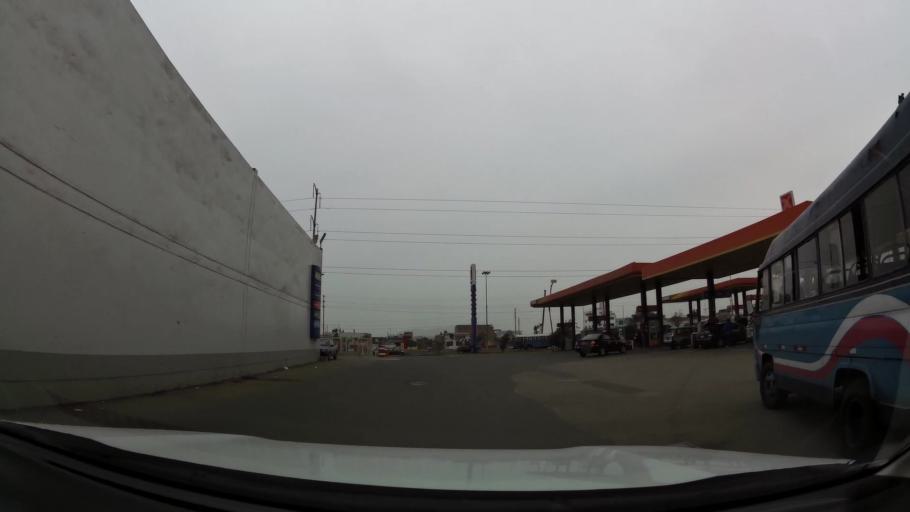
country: PE
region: Lima
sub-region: Lima
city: Surco
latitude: -12.1735
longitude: -76.9774
